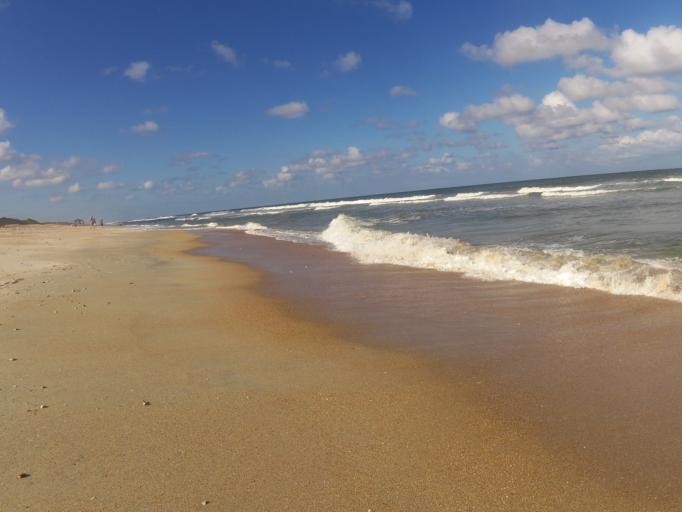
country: US
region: Florida
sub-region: Saint Johns County
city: Palm Valley
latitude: 30.0835
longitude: -81.3365
